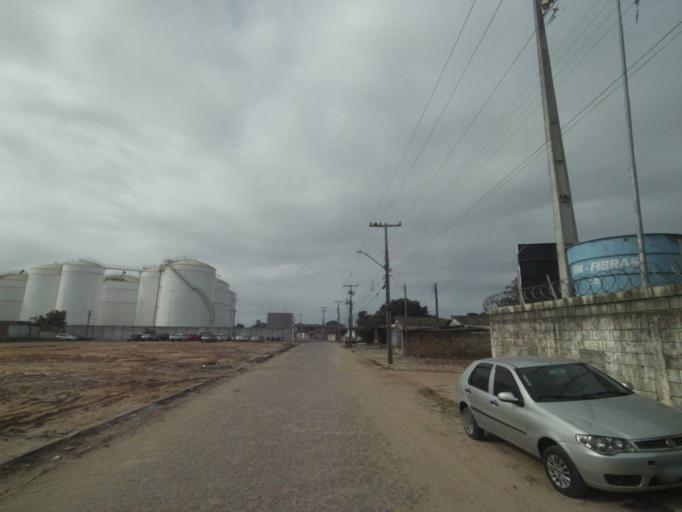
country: BR
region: Parana
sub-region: Paranagua
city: Paranagua
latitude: -25.5128
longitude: -48.5317
